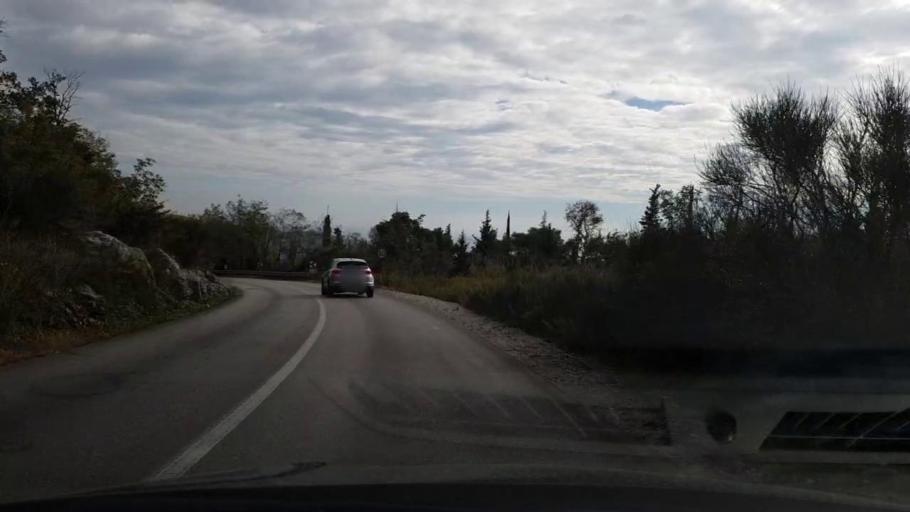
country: ME
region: Herceg Novi
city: Herceg-Novi
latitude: 42.4727
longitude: 18.5351
